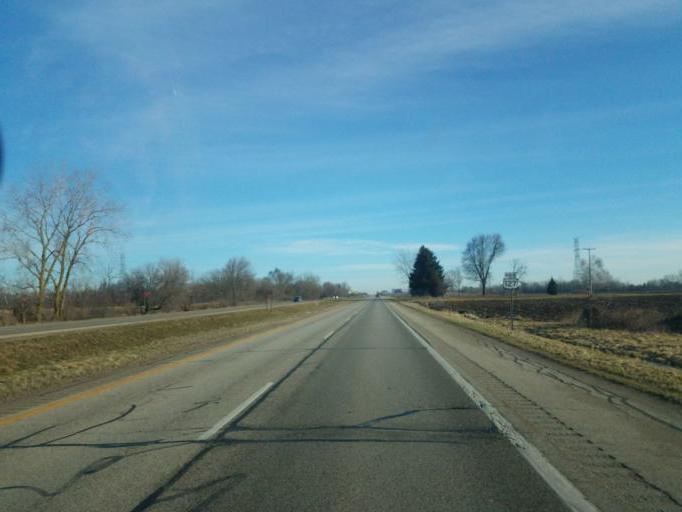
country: US
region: Michigan
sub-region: Gratiot County
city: Ithaca
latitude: 43.2049
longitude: -84.5632
